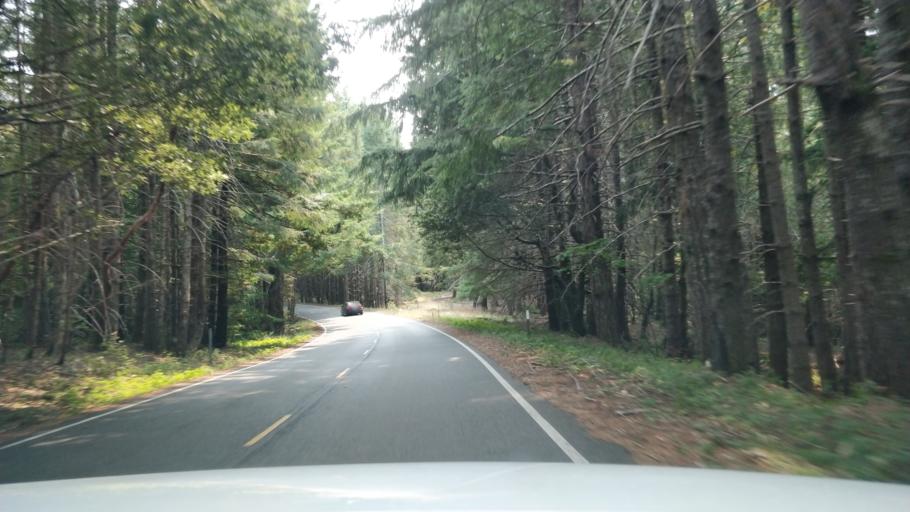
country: US
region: California
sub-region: Humboldt County
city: Westhaven-Moonstone
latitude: 41.2114
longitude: -123.9566
